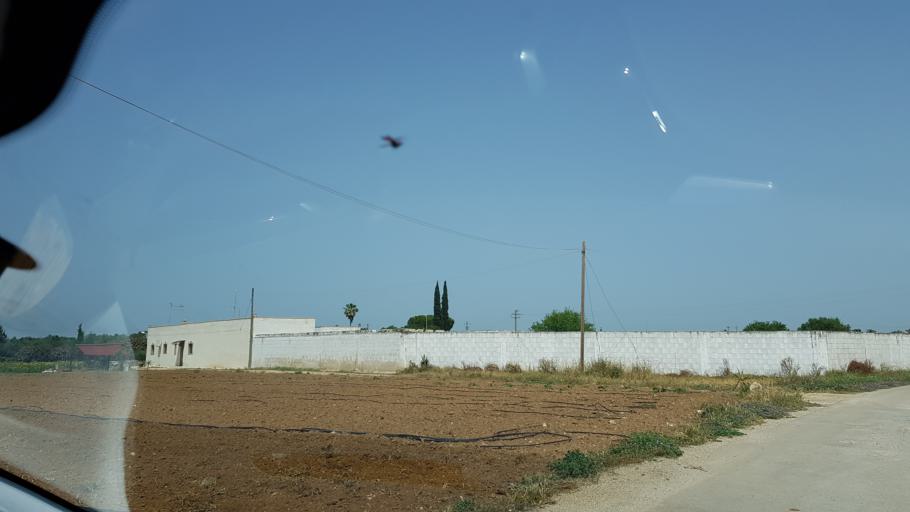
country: IT
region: Apulia
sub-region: Provincia di Brindisi
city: Mesagne
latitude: 40.5530
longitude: 17.8266
